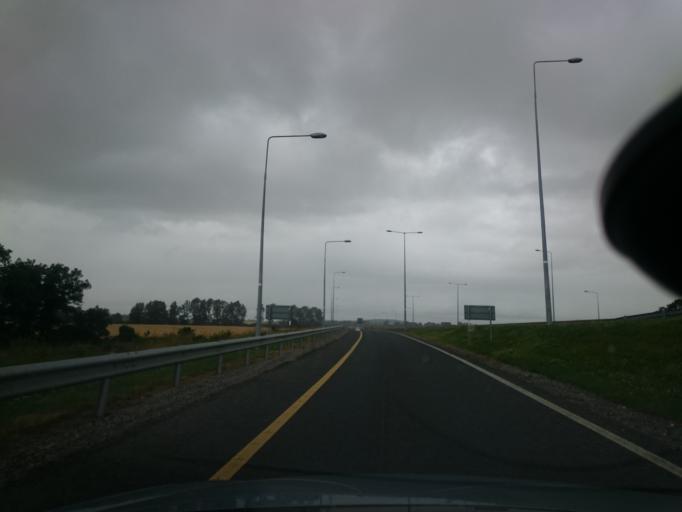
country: IE
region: Leinster
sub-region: Kildare
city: Castledermot
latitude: 52.8939
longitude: -6.8586
